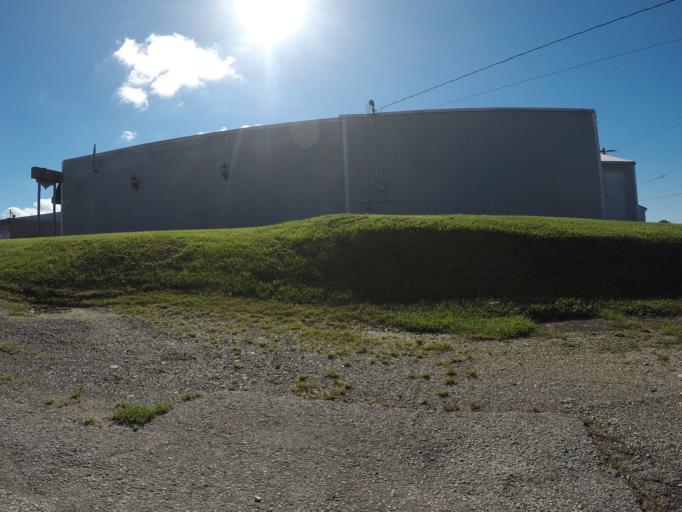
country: US
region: West Virginia
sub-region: Cabell County
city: Huntington
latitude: 38.4133
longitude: -82.4805
